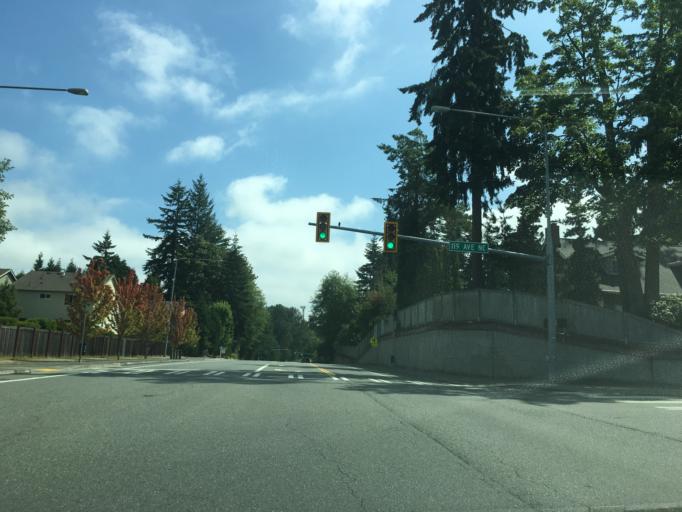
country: US
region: Washington
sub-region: King County
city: Kingsgate
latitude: 47.7438
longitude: -122.1821
